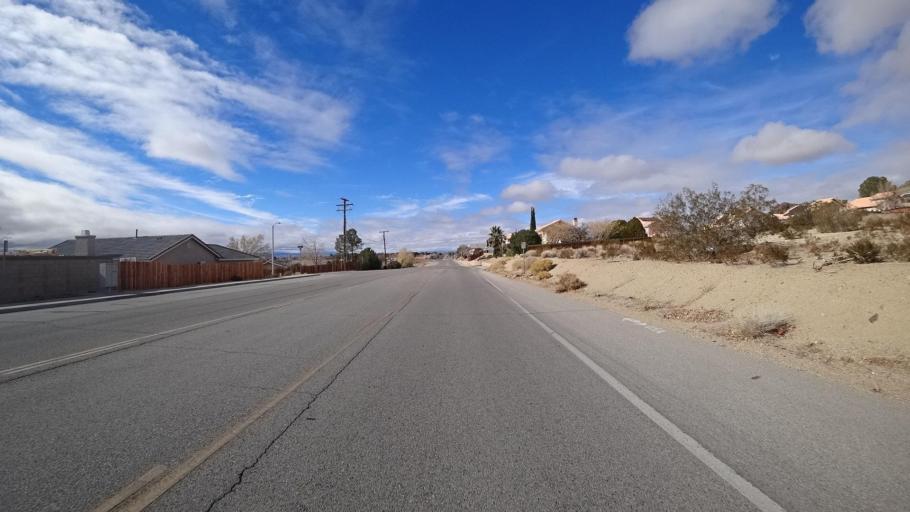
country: US
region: California
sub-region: Kern County
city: Rosamond
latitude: 34.8714
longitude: -118.1797
